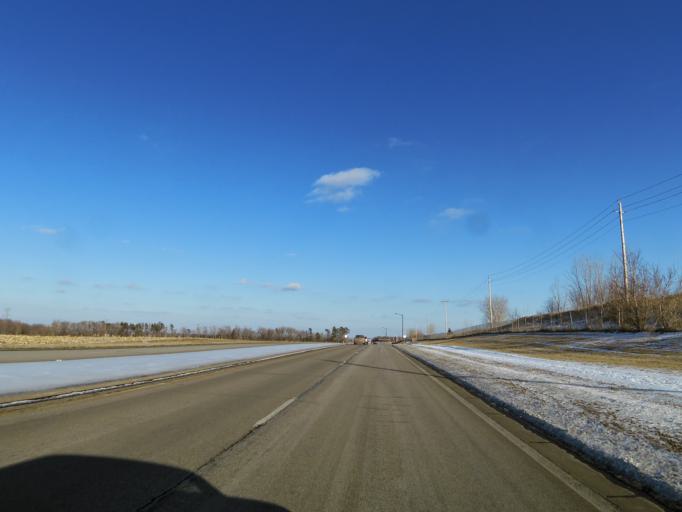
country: US
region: Minnesota
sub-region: Scott County
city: Shakopee
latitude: 44.7757
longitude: -93.4781
